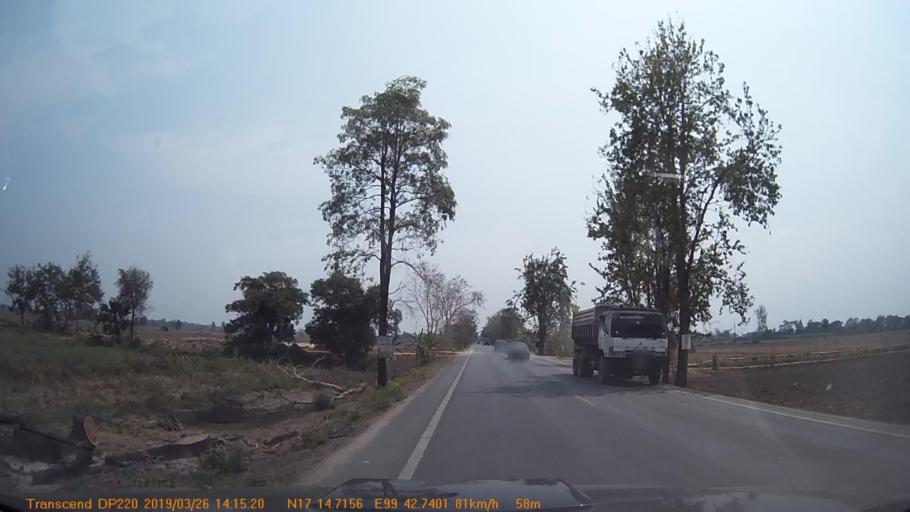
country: TH
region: Sukhothai
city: Sawankhalok
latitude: 17.2450
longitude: 99.7122
